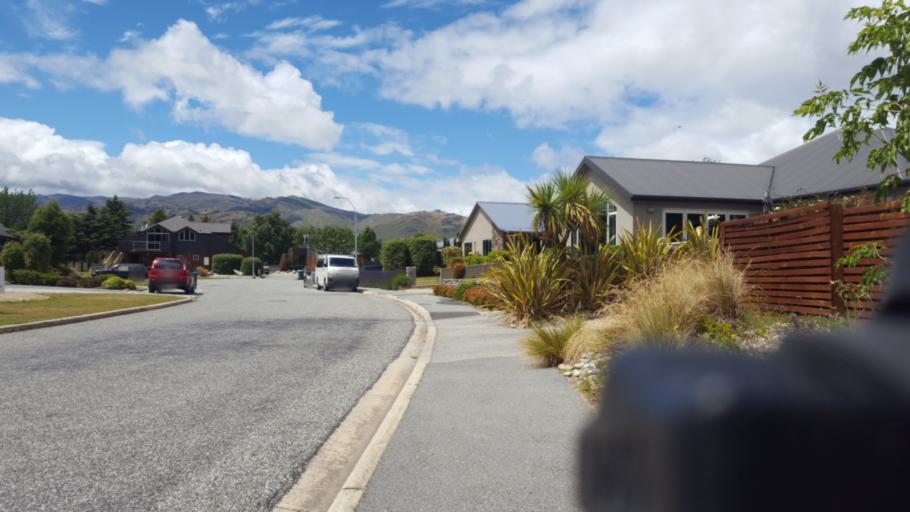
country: NZ
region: Otago
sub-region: Queenstown-Lakes District
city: Wanaka
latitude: -45.0422
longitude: 169.1809
